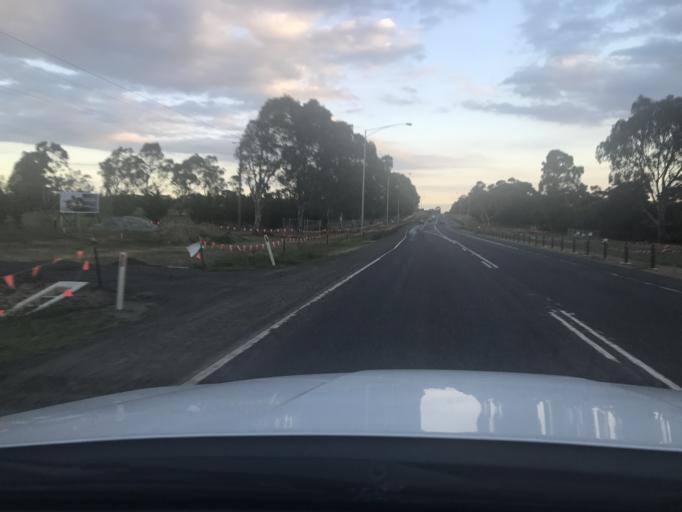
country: AU
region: Victoria
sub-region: Hume
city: Greenvale
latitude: -37.5957
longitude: 144.8811
